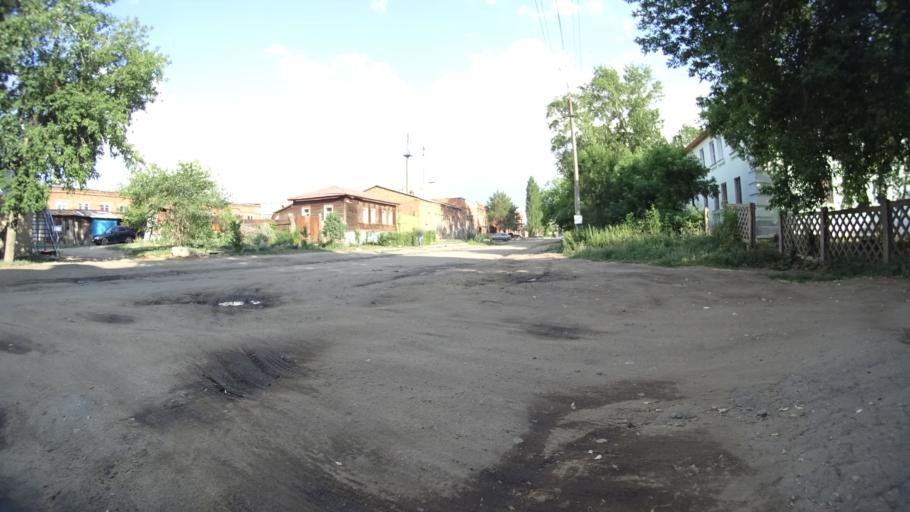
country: RU
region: Chelyabinsk
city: Troitsk
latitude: 54.0863
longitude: 61.5441
